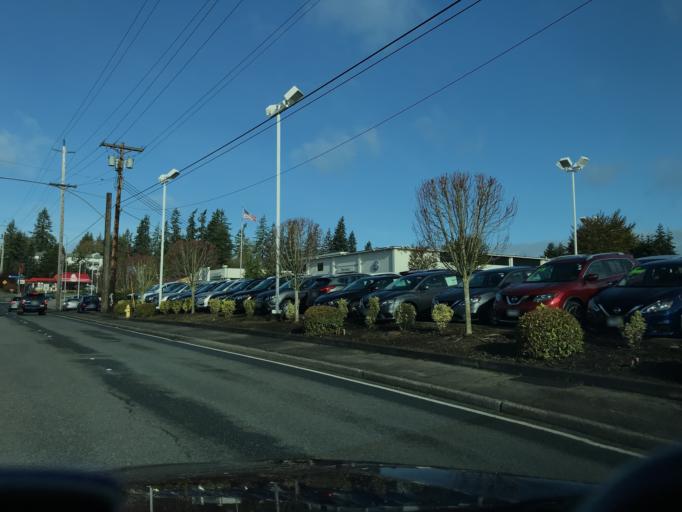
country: US
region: Washington
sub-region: Snohomish County
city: Esperance
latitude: 47.7778
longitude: -122.3444
